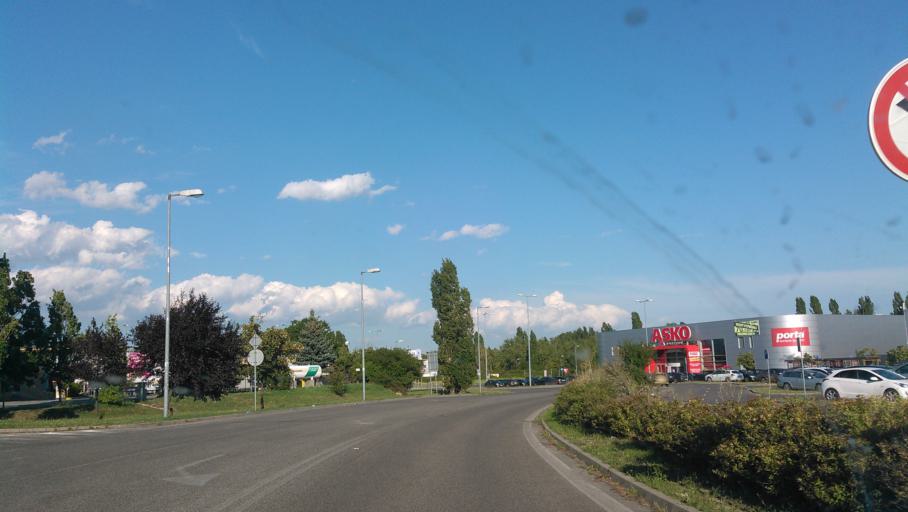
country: SK
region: Bratislavsky
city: Svaty Jur
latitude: 48.1879
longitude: 17.1787
